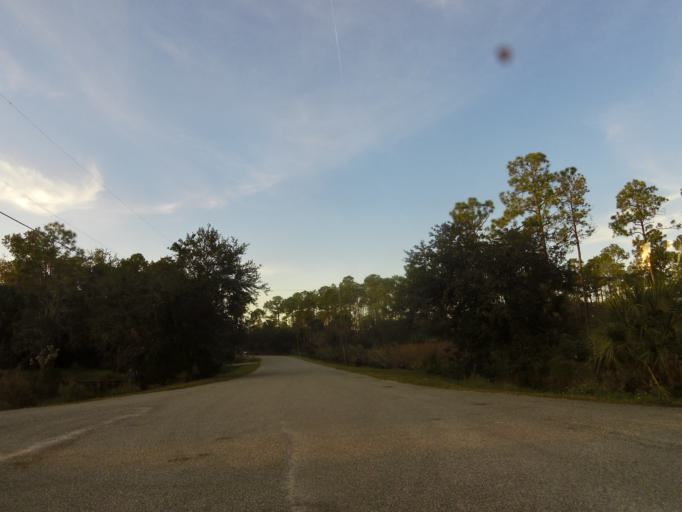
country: US
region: Florida
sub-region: Saint Johns County
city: Palm Valley
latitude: 30.1287
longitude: -81.3800
